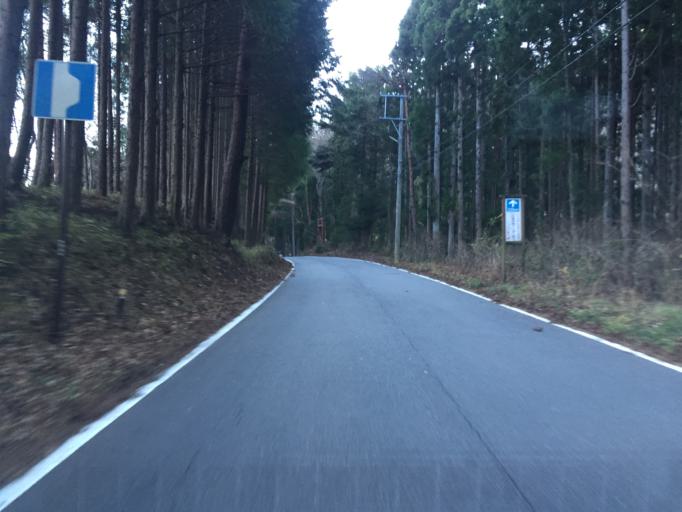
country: JP
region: Fukushima
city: Iwaki
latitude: 37.1850
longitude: 140.8164
